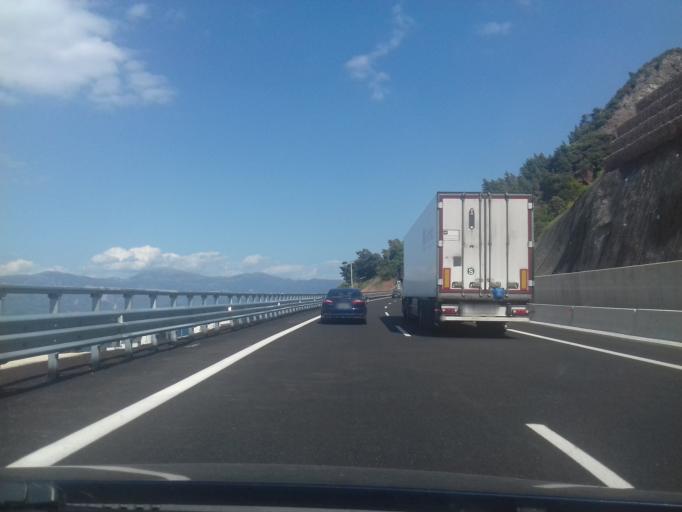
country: GR
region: West Greece
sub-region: Nomos Achaias
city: Kamarai
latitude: 38.3236
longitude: 21.9092
